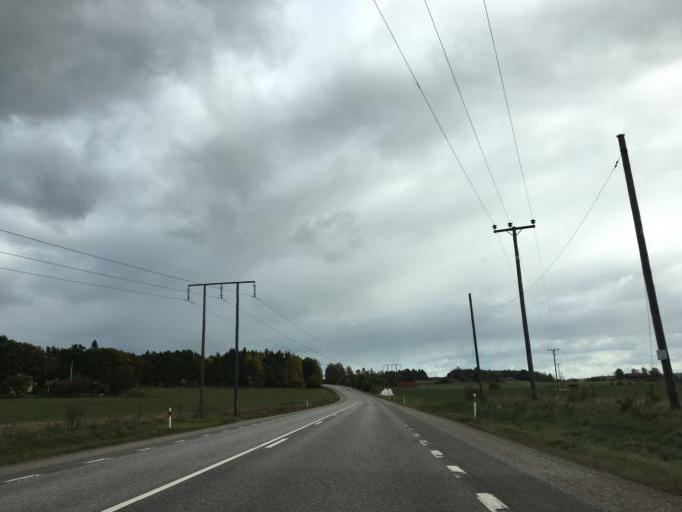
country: SE
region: Soedermanland
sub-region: Nykopings Kommun
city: Svalsta
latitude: 58.7744
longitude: 16.8866
